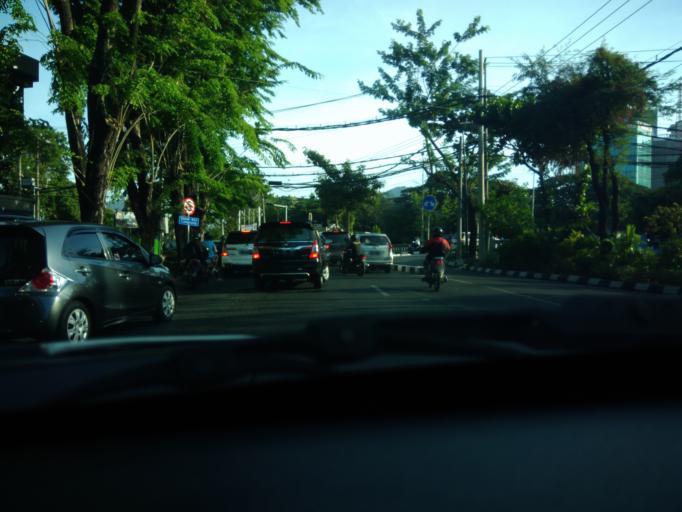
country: ID
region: East Java
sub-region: Kota Surabaya
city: Surabaya
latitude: -7.2553
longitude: 112.7436
